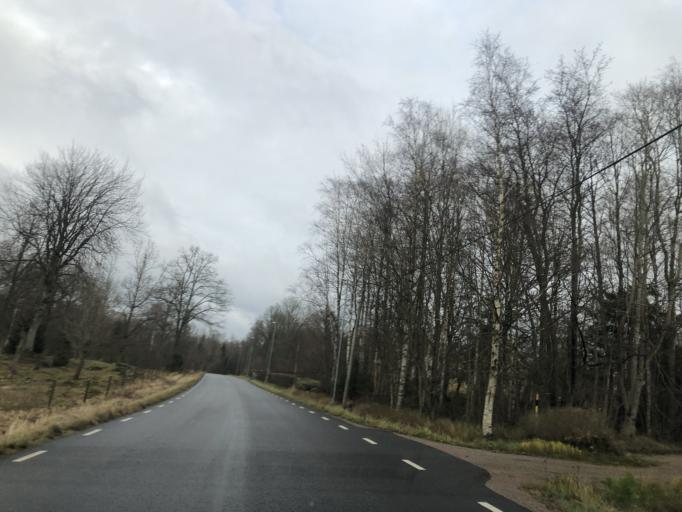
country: SE
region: Vaestra Goetaland
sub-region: Ulricehamns Kommun
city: Ulricehamn
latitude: 57.8307
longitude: 13.2572
